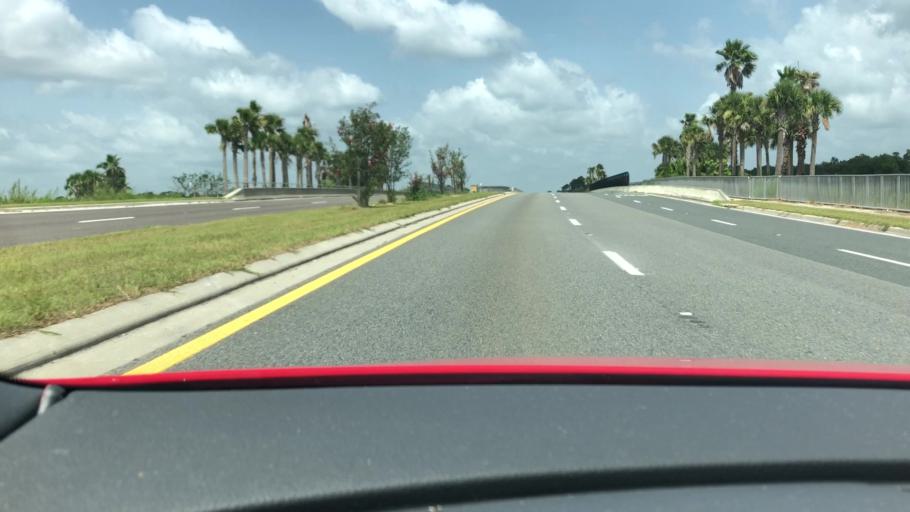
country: US
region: Florida
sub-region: Volusia County
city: Lake Helen
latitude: 29.0175
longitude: -81.2298
